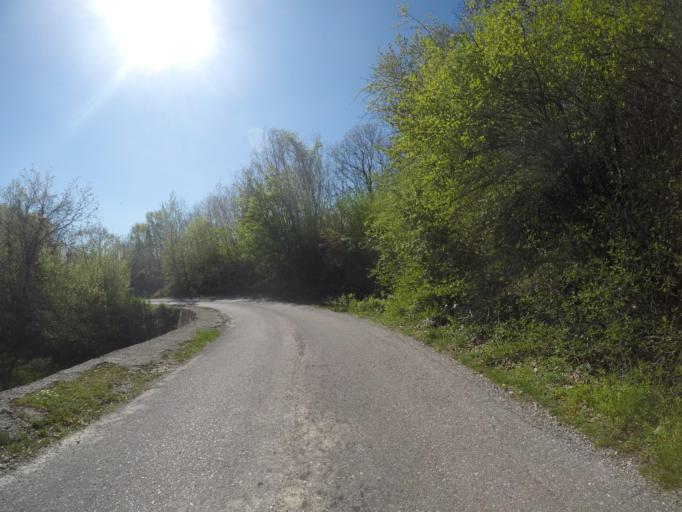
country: ME
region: Danilovgrad
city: Danilovgrad
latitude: 42.5169
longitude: 19.0529
